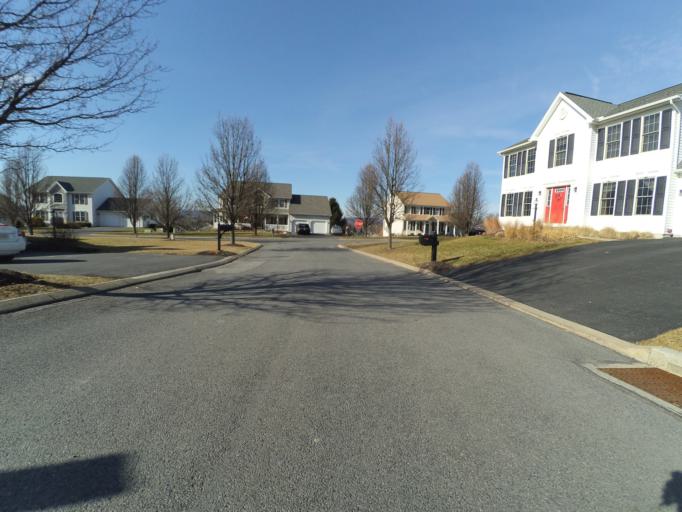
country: US
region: Pennsylvania
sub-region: Centre County
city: Lemont
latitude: 40.8212
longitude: -77.8040
